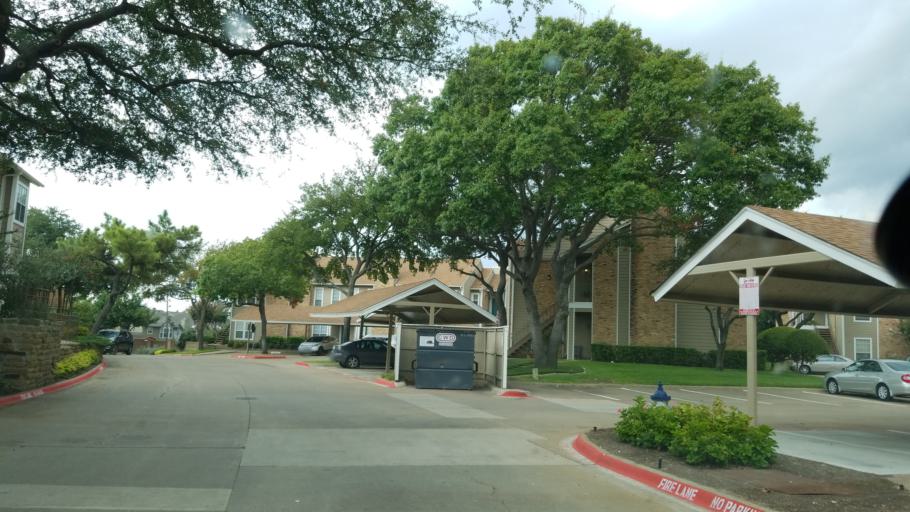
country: US
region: Texas
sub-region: Dallas County
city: Richardson
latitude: 32.8979
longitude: -96.7256
